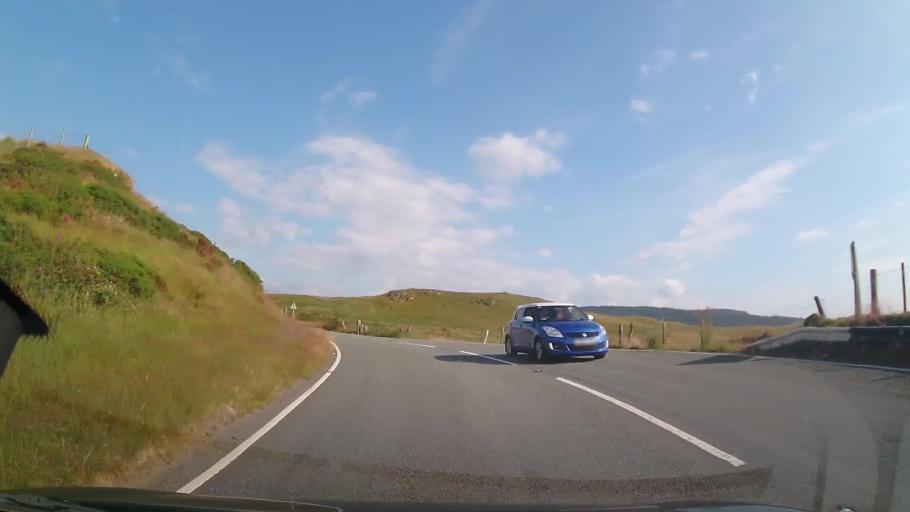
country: GB
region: Wales
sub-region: Gwynedd
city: Ffestiniog
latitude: 52.9603
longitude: -3.8950
